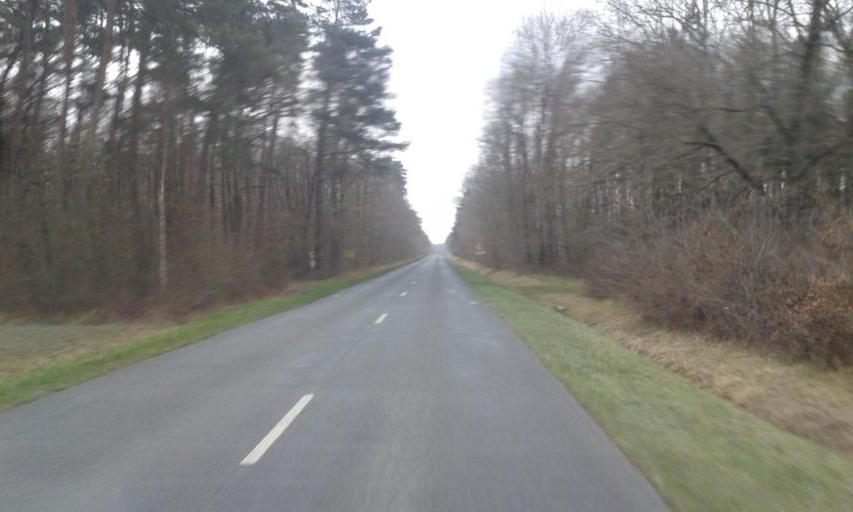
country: FR
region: Centre
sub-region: Departement du Loir-et-Cher
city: Dhuizon
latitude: 47.6106
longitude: 1.6610
